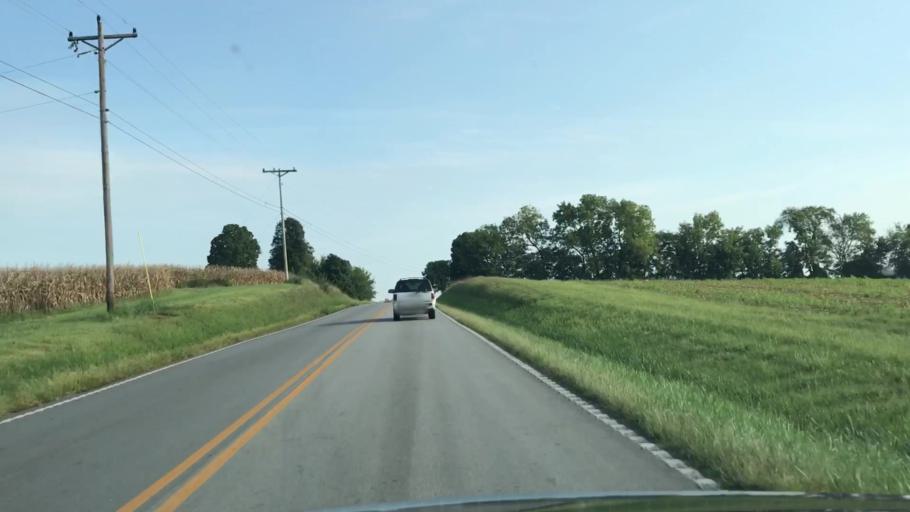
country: US
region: Kentucky
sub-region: Todd County
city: Guthrie
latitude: 36.6576
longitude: -87.1994
